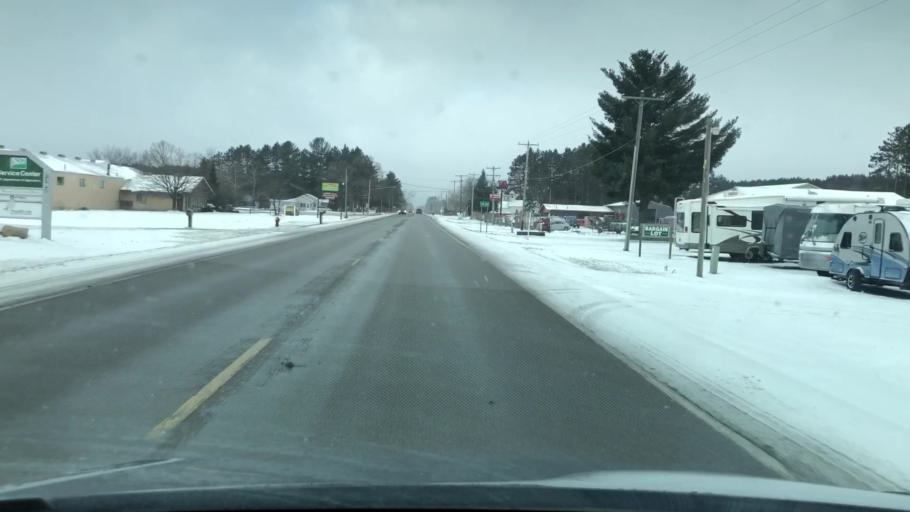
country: US
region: Michigan
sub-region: Wexford County
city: Cadillac
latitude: 44.2813
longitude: -85.4342
